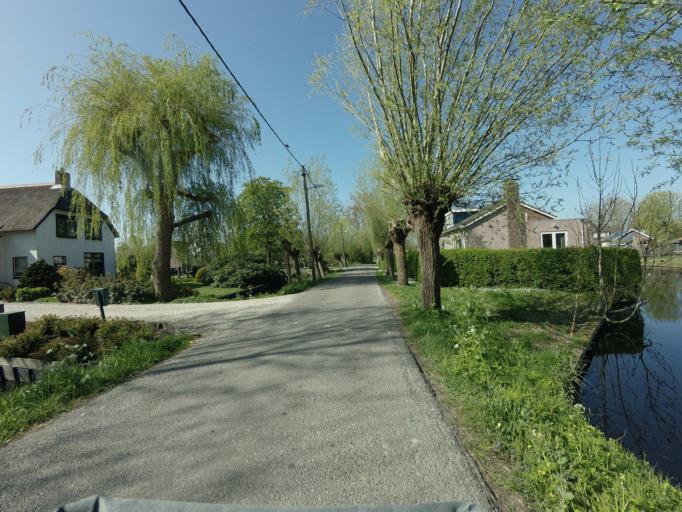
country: NL
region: Utrecht
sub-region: Gemeente Oudewater
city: Oudewater
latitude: 52.0515
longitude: 4.8128
